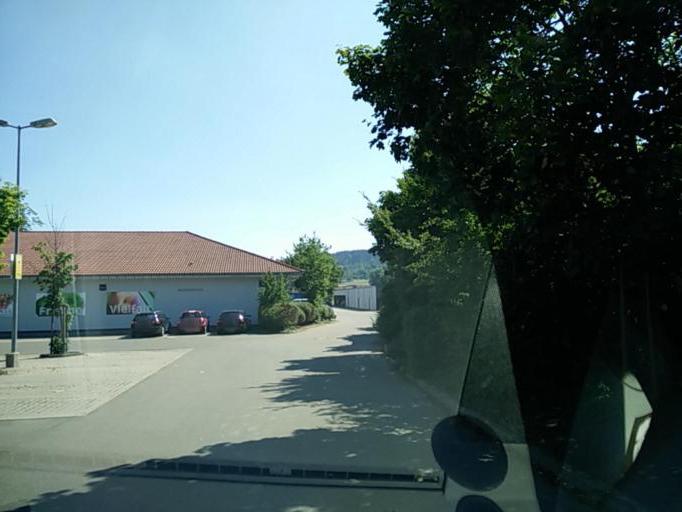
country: DE
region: Baden-Wuerttemberg
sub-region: Tuebingen Region
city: Rottenburg
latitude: 48.5313
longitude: 8.9618
